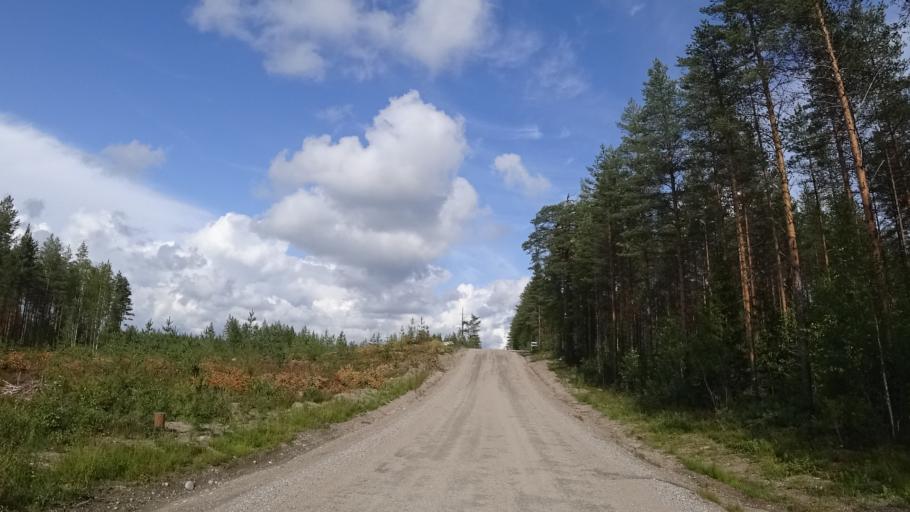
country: FI
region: North Karelia
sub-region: Pielisen Karjala
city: Lieksa
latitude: 63.5734
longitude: 30.1165
